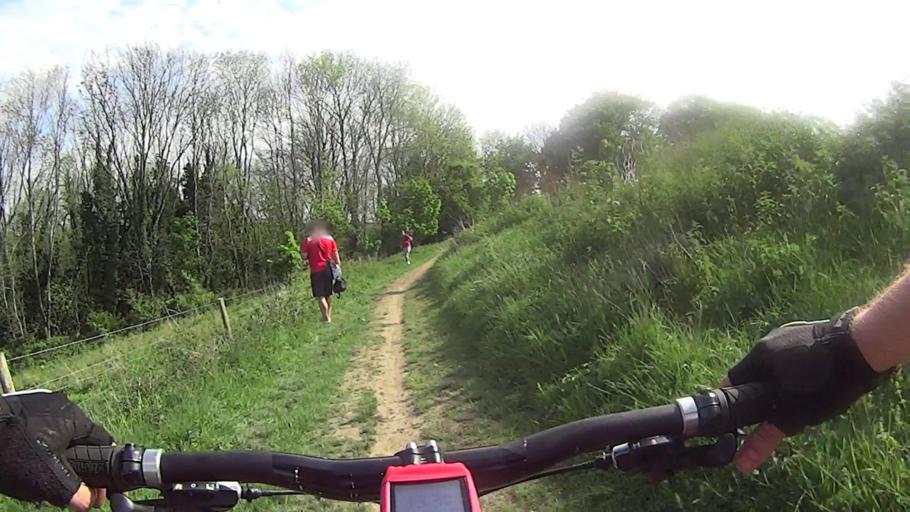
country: GB
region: England
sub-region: West Sussex
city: Milland
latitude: 50.9572
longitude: -0.8379
